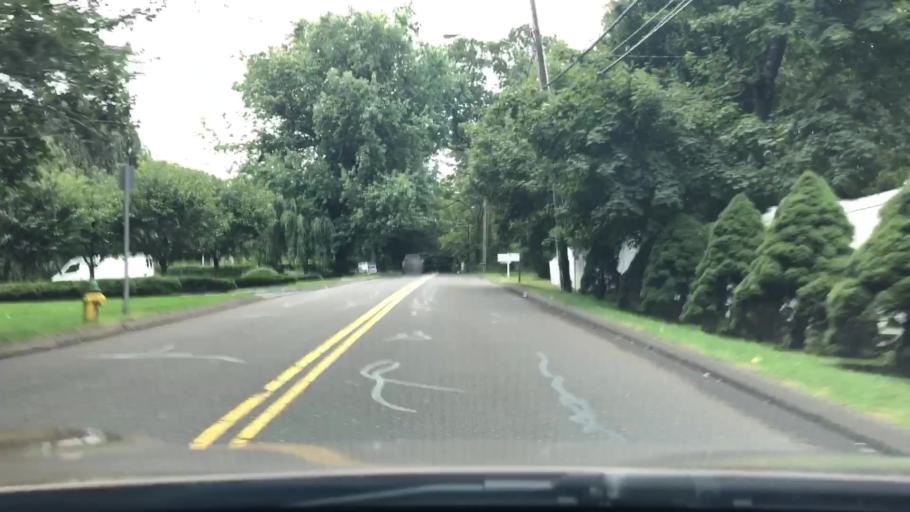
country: US
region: Connecticut
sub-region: Fairfield County
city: New Canaan
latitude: 41.1318
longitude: -73.4554
